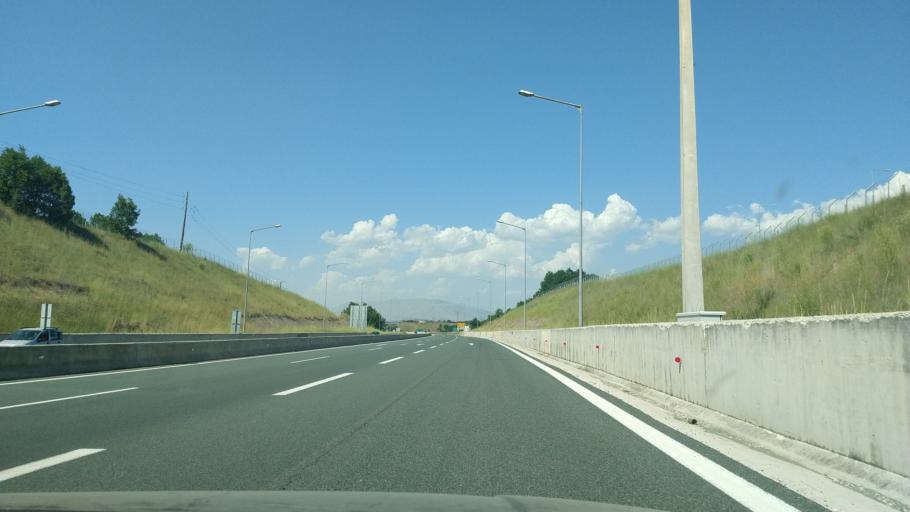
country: GR
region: West Macedonia
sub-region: Nomos Grevenon
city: Grevena
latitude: 40.0686
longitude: 21.4410
